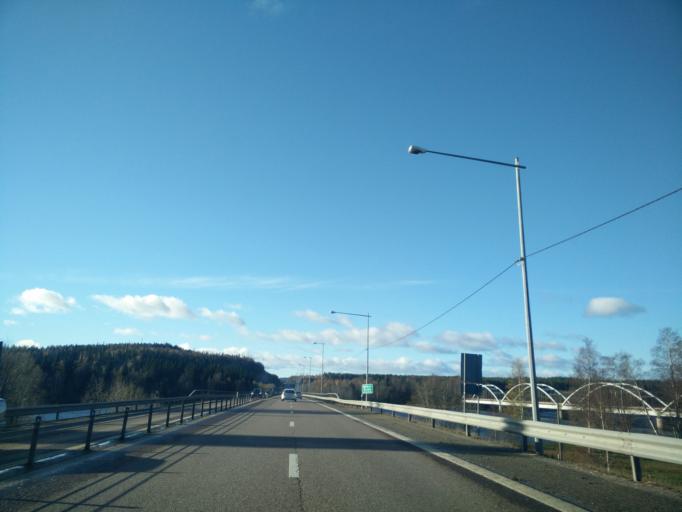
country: SE
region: Vaesternorrland
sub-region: Timra Kommun
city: Bergeforsen
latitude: 62.5182
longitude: 17.4324
